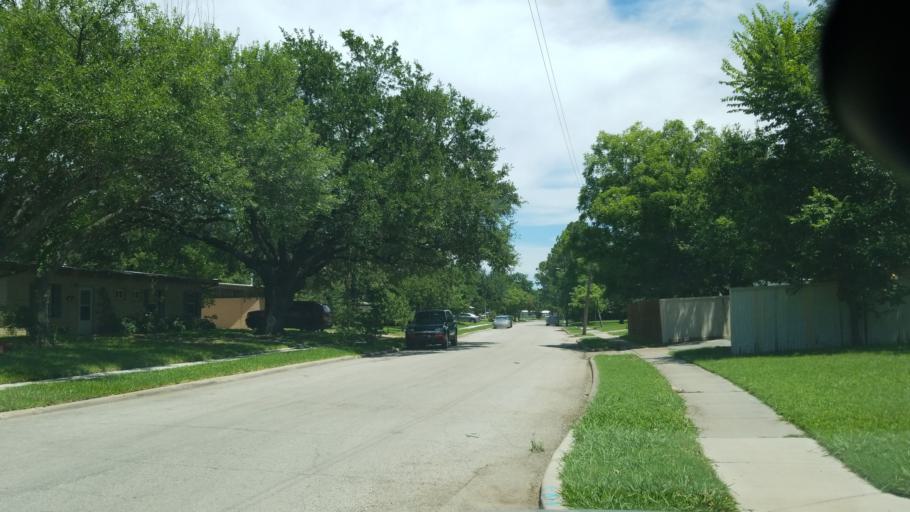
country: US
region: Texas
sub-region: Dallas County
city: Irving
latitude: 32.8334
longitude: -96.9716
